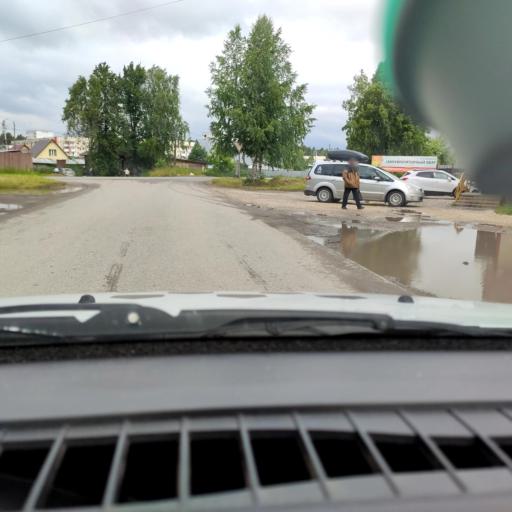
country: RU
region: Perm
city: Dobryanka
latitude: 58.4713
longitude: 56.4113
